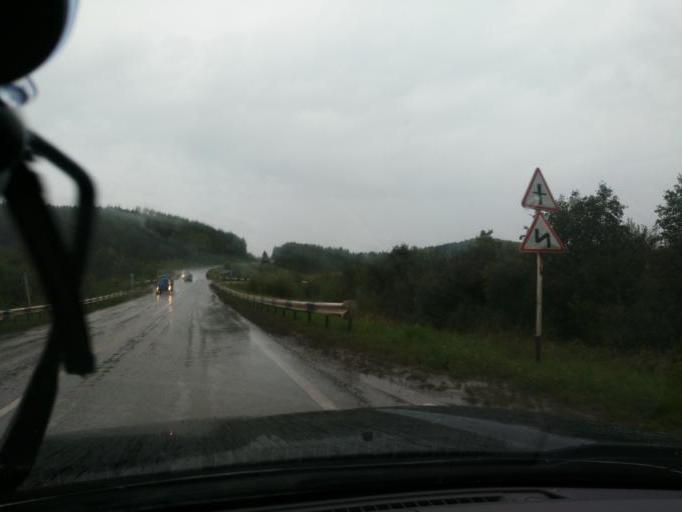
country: RU
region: Perm
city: Osa
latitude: 57.3009
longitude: 55.6154
